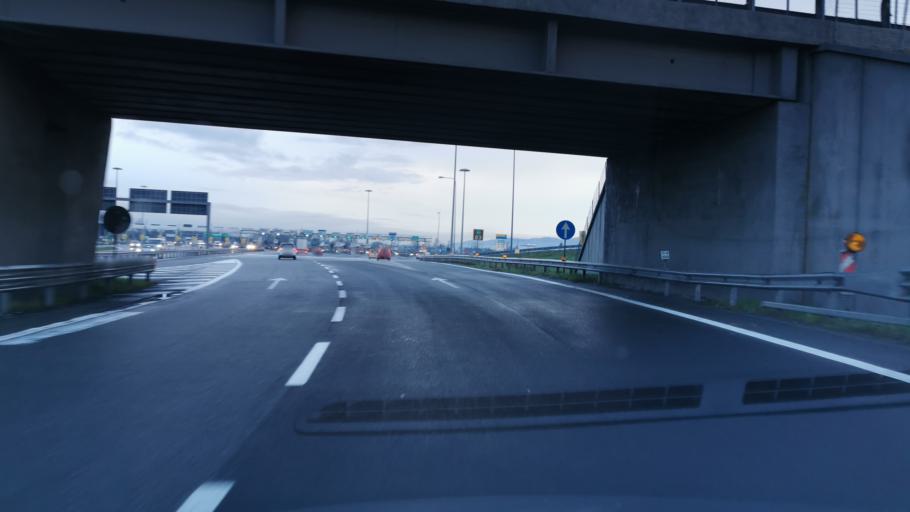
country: IT
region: Piedmont
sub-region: Provincia di Torino
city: Leini
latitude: 45.1324
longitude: 7.7133
